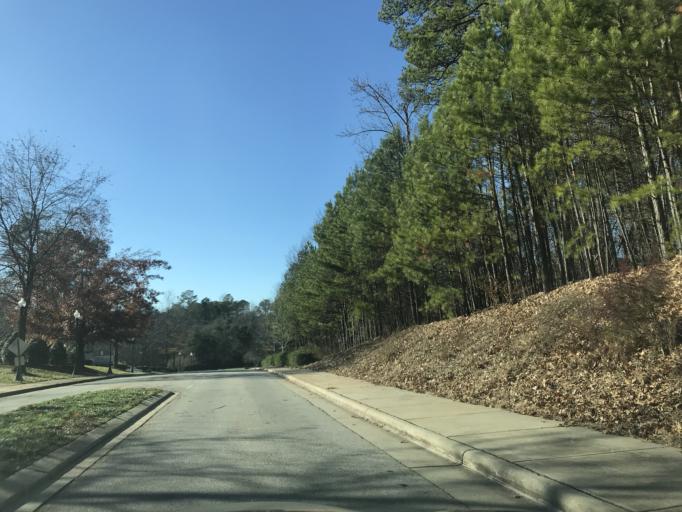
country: US
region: North Carolina
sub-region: Wake County
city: Morrisville
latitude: 35.8821
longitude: -78.8275
